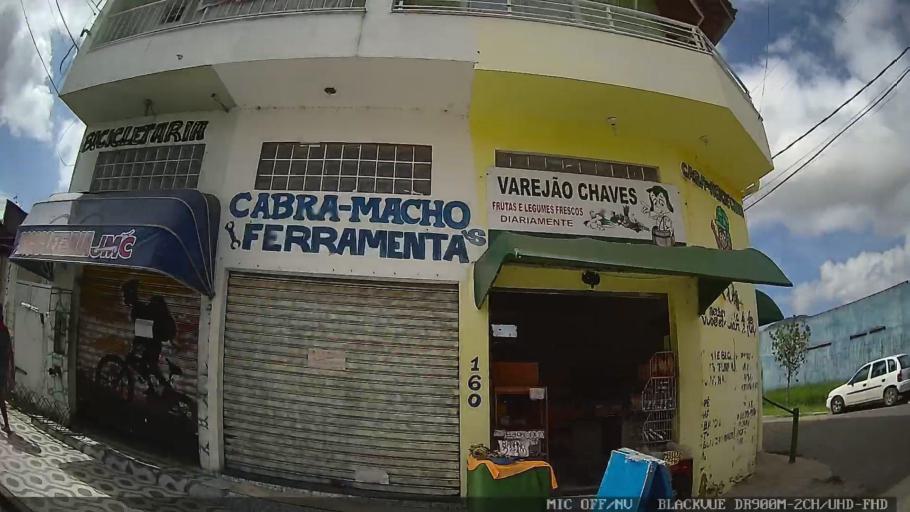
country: BR
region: Sao Paulo
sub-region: Peruibe
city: Peruibe
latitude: -24.2981
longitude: -47.0238
